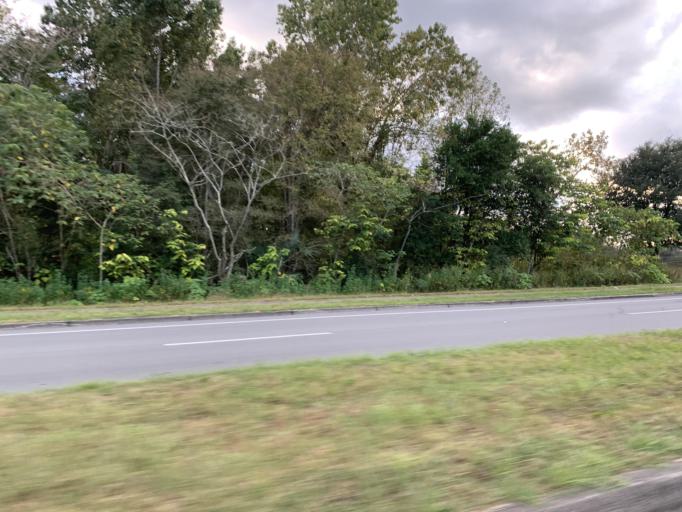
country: US
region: Florida
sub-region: Marion County
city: Ocala
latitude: 29.1566
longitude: -82.1440
